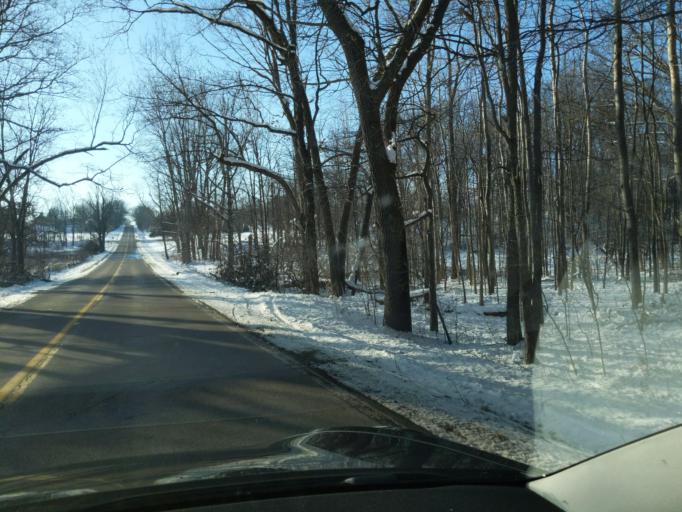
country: US
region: Michigan
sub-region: Ingham County
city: Stockbridge
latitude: 42.4679
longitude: -84.1163
